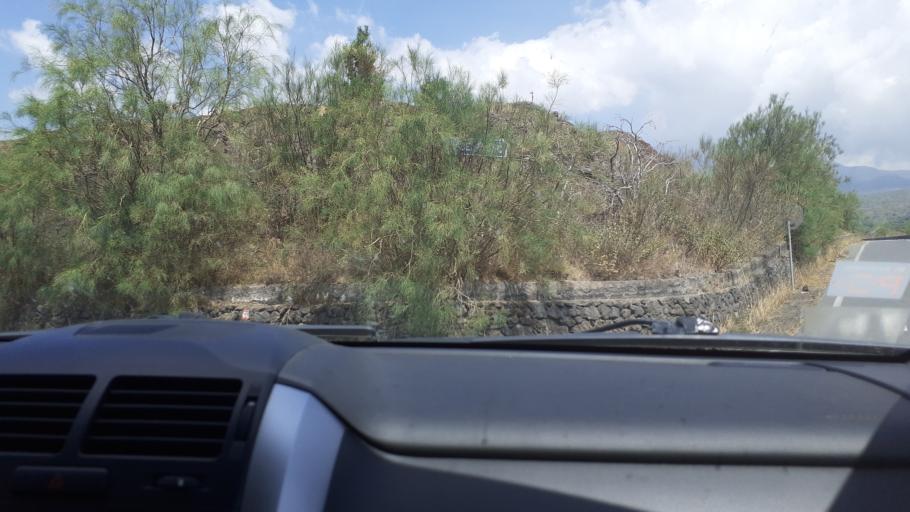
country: IT
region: Sicily
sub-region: Catania
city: Nicolosi
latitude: 37.6476
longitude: 15.0215
